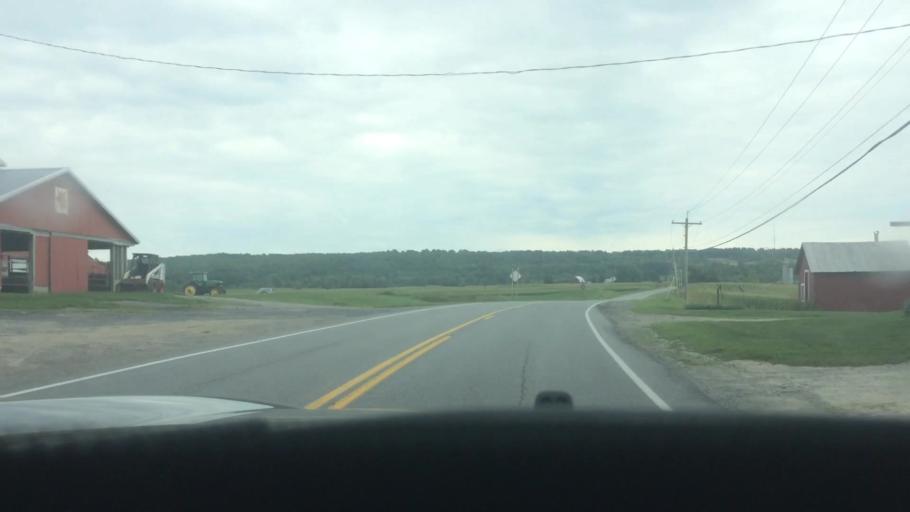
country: US
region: New York
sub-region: St. Lawrence County
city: Canton
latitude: 44.5548
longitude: -75.1113
